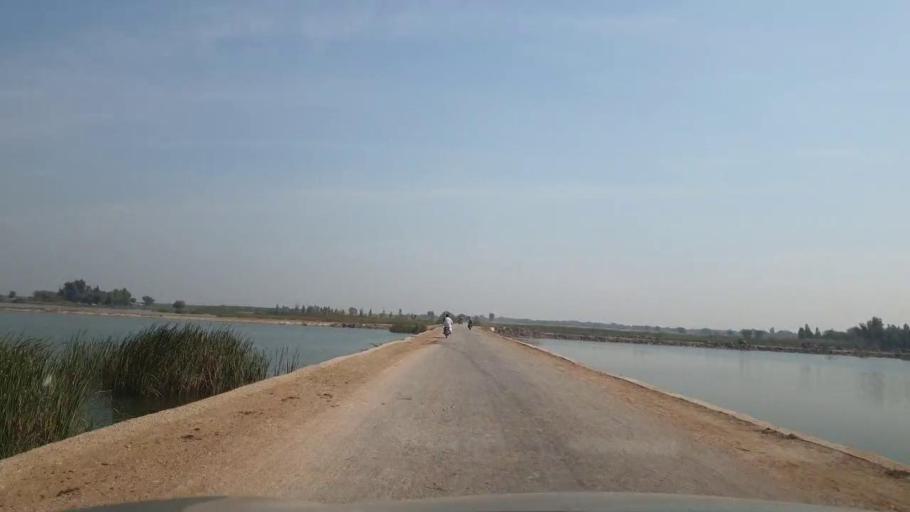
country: PK
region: Sindh
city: Tando Adam
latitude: 25.6284
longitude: 68.7235
